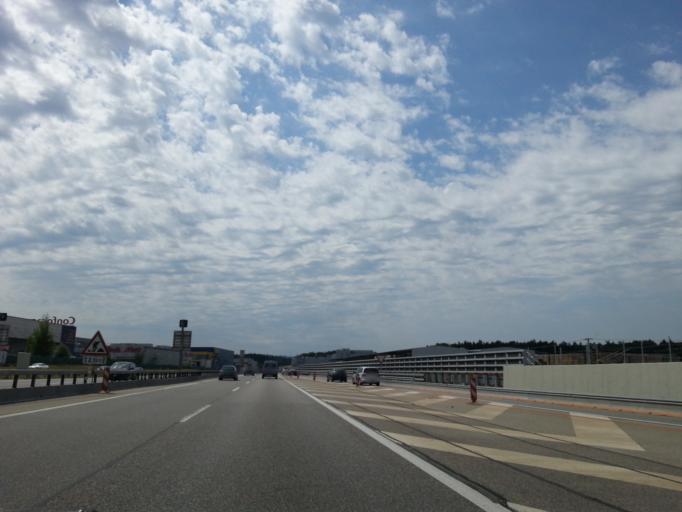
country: CH
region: Bern
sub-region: Emmental District
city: Kirchberg
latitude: 47.0791
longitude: 7.5716
